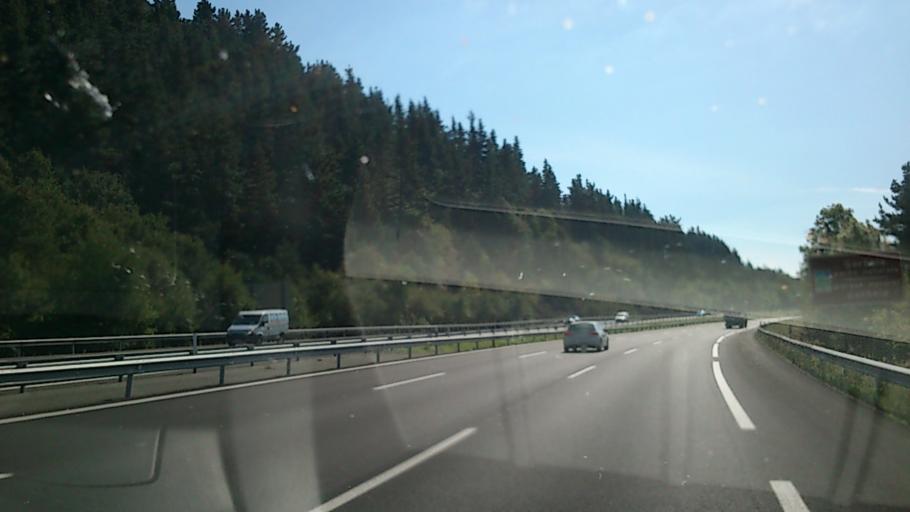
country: ES
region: Basque Country
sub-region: Provincia de Alava
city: Lezama
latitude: 43.0291
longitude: -2.9120
